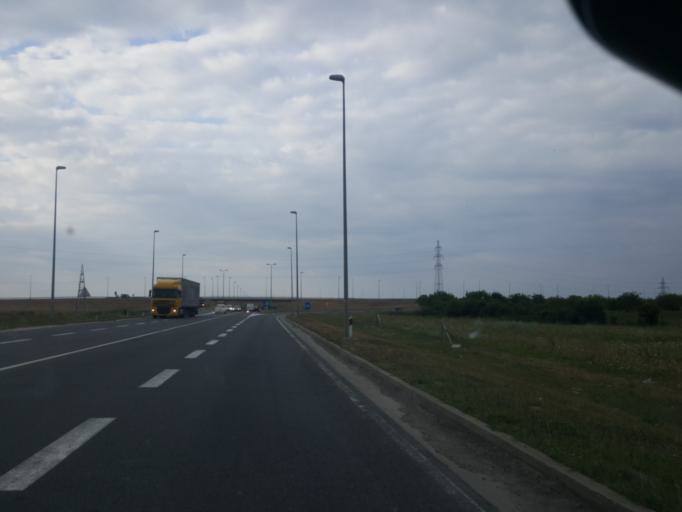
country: RS
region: Autonomna Pokrajina Vojvodina
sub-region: Juznobacki Okrug
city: Novi Sad
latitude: 45.3024
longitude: 19.8081
